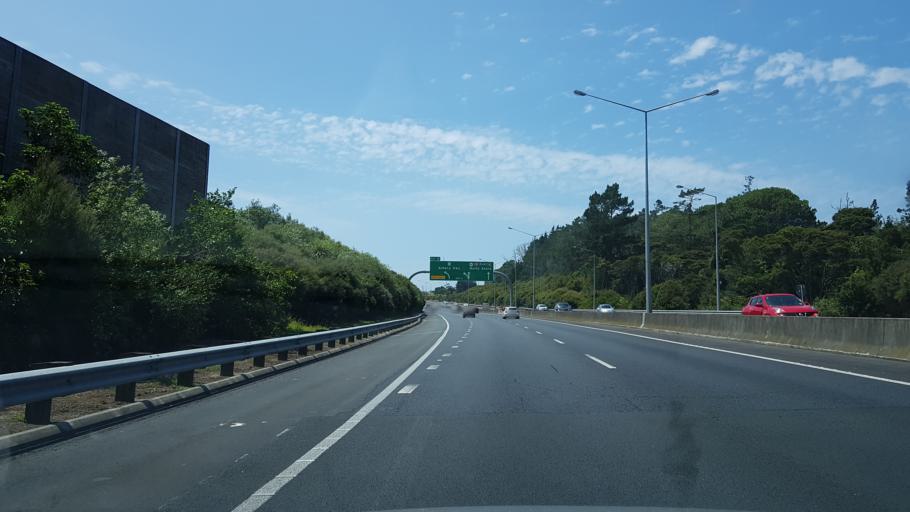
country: NZ
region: Auckland
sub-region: Auckland
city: Rothesay Bay
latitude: -36.7634
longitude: 174.6973
